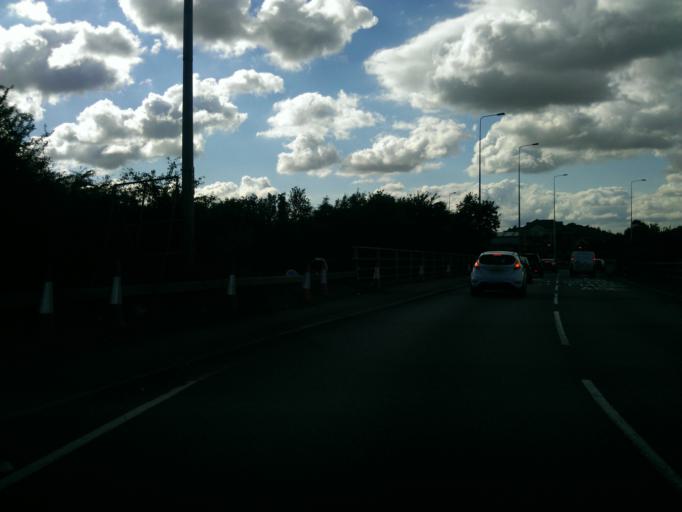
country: GB
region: England
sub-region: Warwickshire
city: Kingsbury
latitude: 52.6022
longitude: -1.6420
